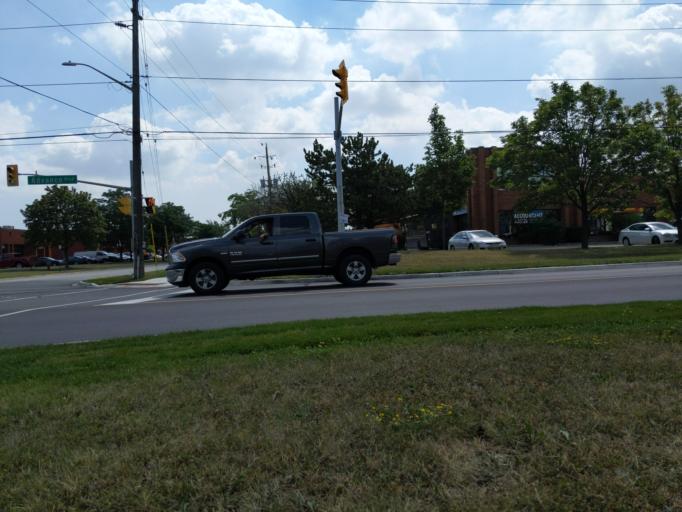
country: CA
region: Ontario
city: Brampton
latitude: 43.6895
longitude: -79.6973
